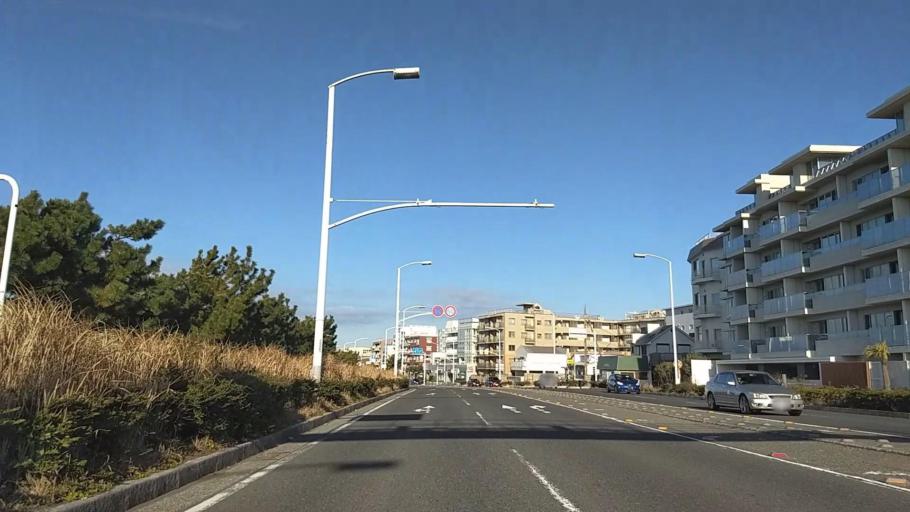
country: JP
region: Kanagawa
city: Fujisawa
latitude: 35.3127
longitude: 139.4773
